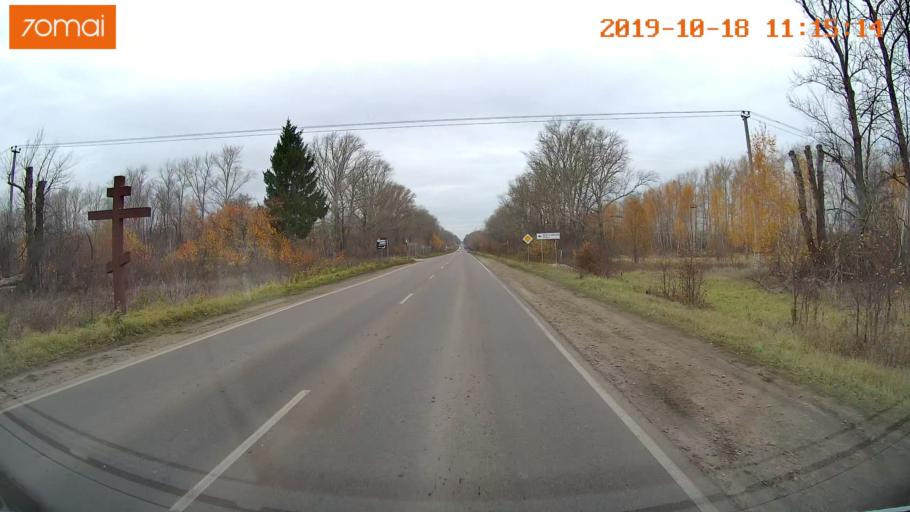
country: RU
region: Tula
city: Kimovsk
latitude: 53.9906
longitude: 38.5473
